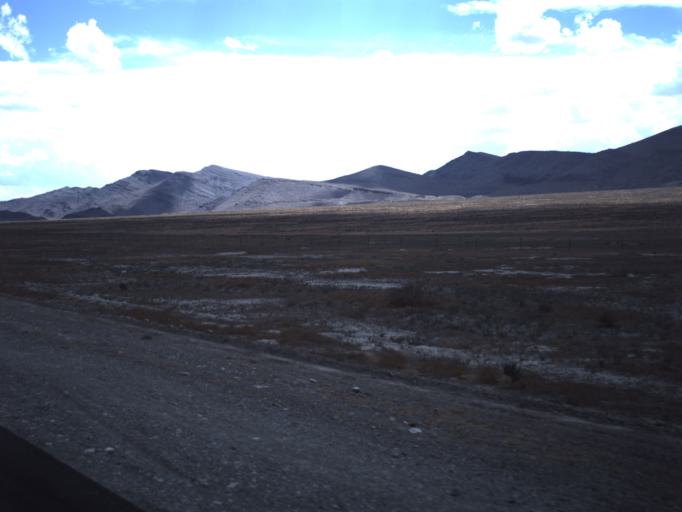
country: US
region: Utah
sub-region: Beaver County
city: Milford
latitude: 39.0768
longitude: -113.4782
